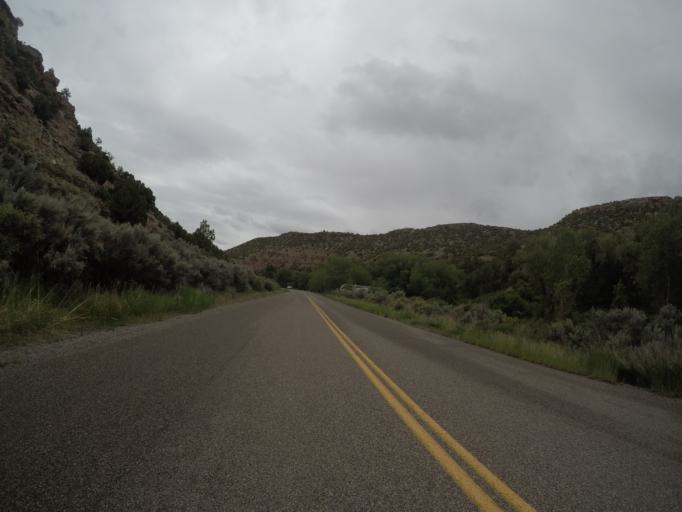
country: US
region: Wyoming
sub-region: Big Horn County
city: Lovell
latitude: 45.1054
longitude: -108.2257
